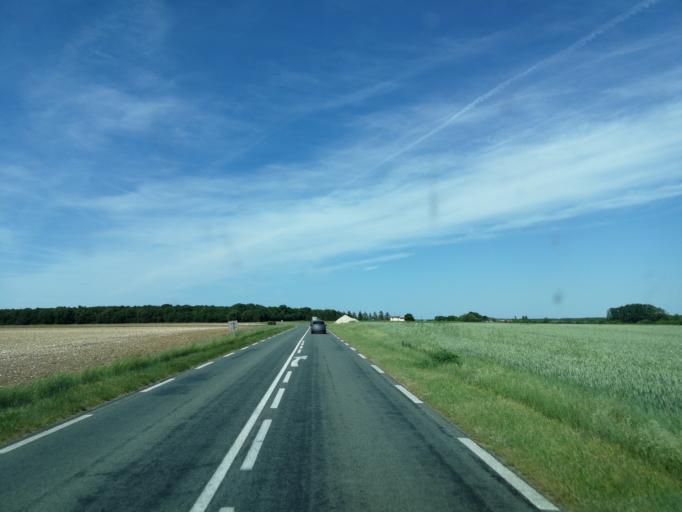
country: FR
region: Poitou-Charentes
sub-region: Departement de la Vienne
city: Loudun
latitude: 47.0371
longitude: 0.1246
